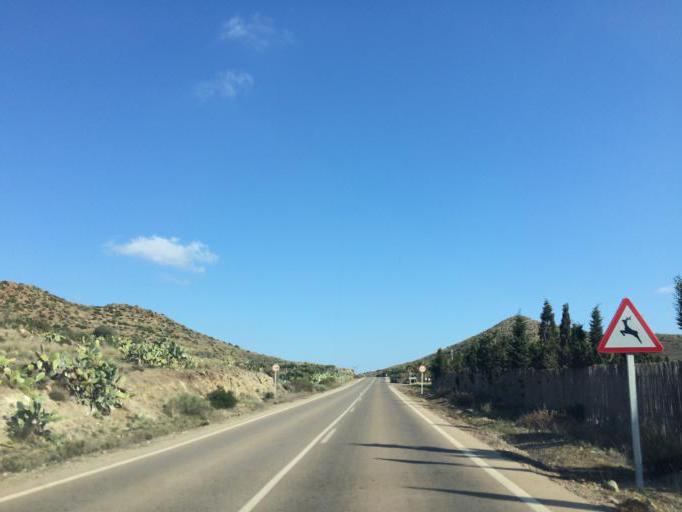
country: ES
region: Andalusia
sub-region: Provincia de Almeria
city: San Jose
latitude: 36.7948
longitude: -2.1119
